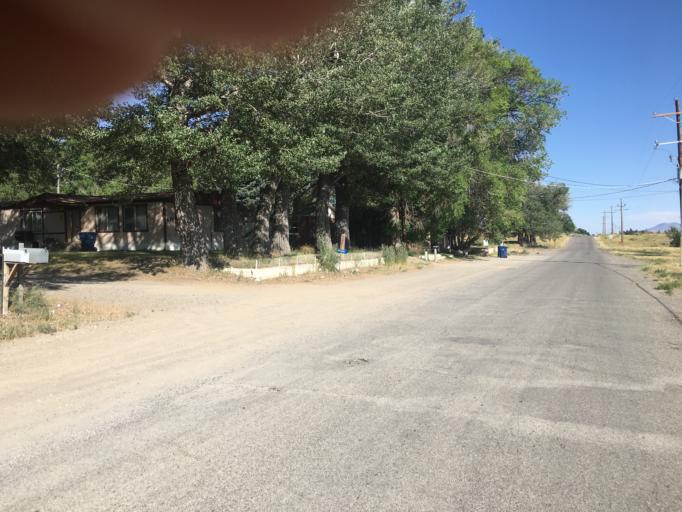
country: US
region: Idaho
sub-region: Butte County
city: Arco
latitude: 43.6331
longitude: -113.2943
